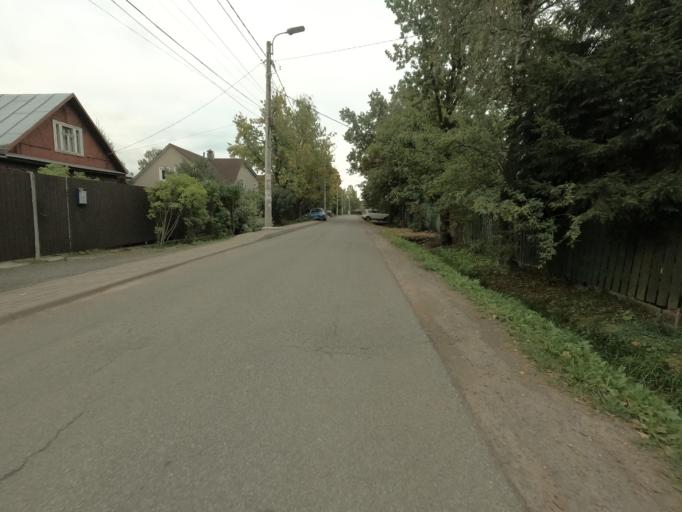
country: RU
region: St.-Petersburg
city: Ust'-Izhora
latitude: 59.8127
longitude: 30.5864
